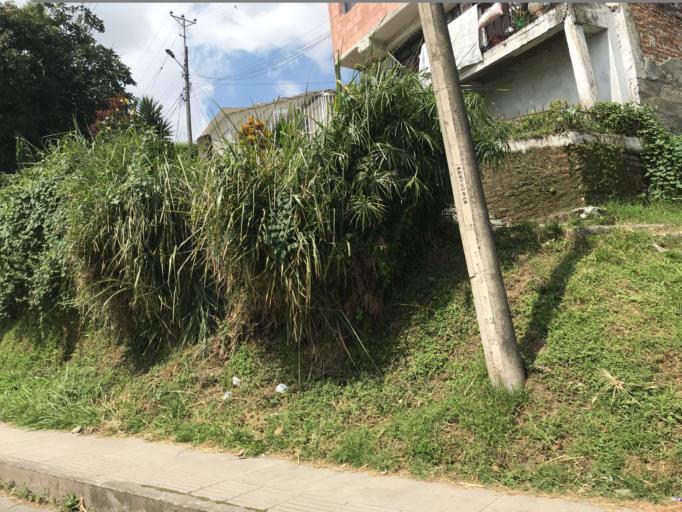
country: CO
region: Quindio
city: Calarca
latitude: 4.5236
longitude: -75.6396
